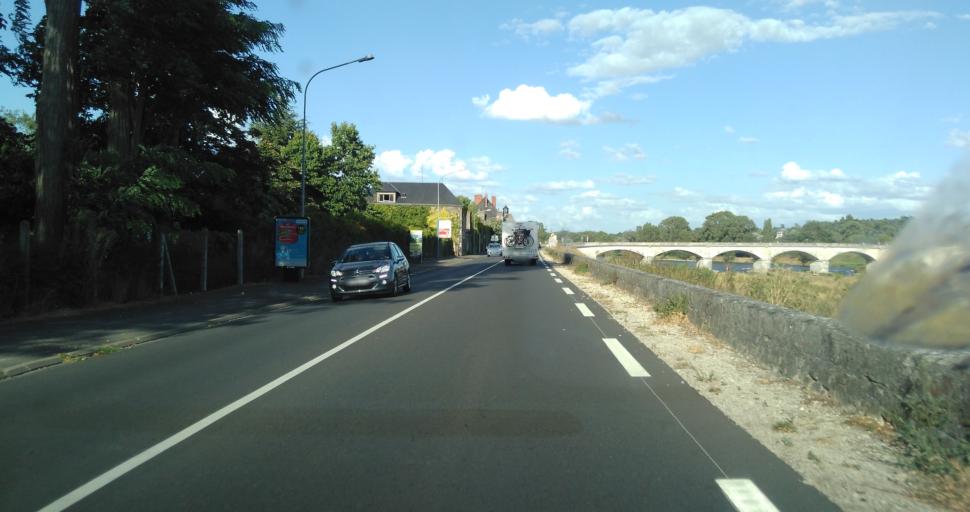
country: FR
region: Centre
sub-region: Departement d'Indre-et-Loire
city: Amboise
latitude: 47.4165
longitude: 0.9774
